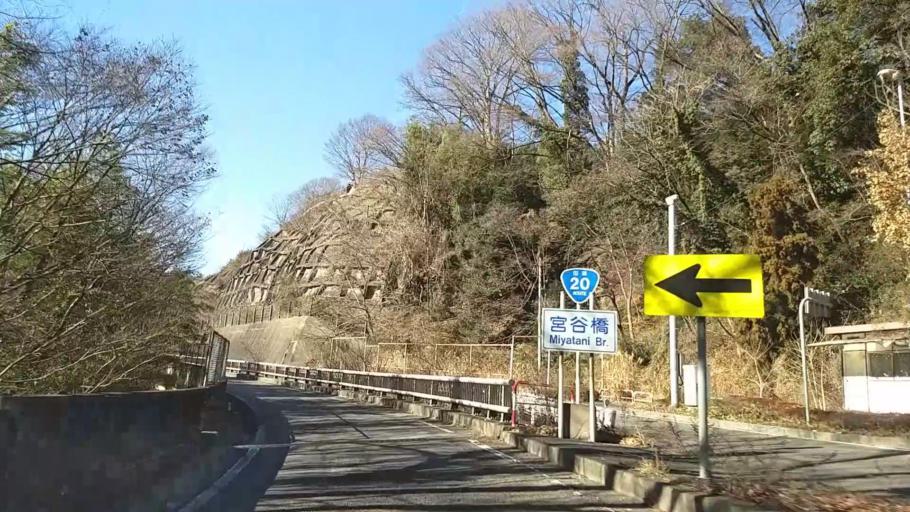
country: JP
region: Yamanashi
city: Otsuki
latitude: 35.6175
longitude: 138.9904
